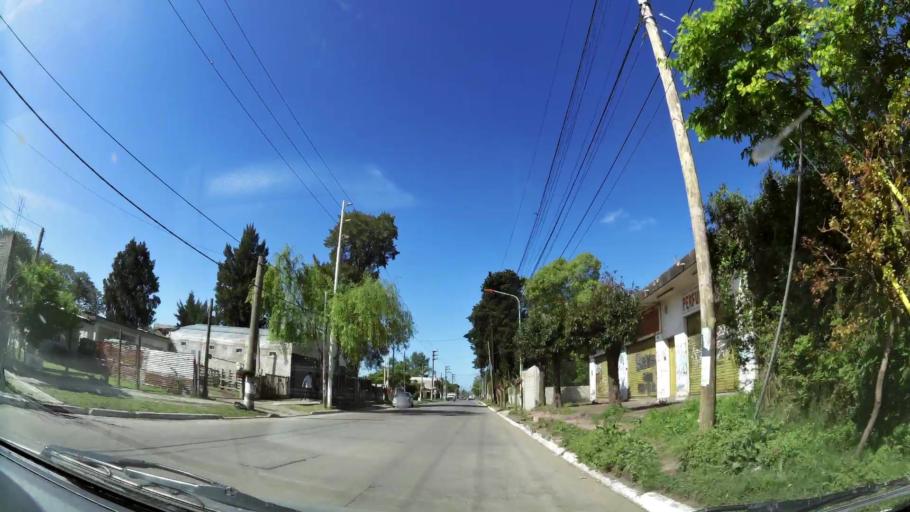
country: AR
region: Buenos Aires
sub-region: Partido de Quilmes
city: Quilmes
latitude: -34.7990
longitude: -58.2617
